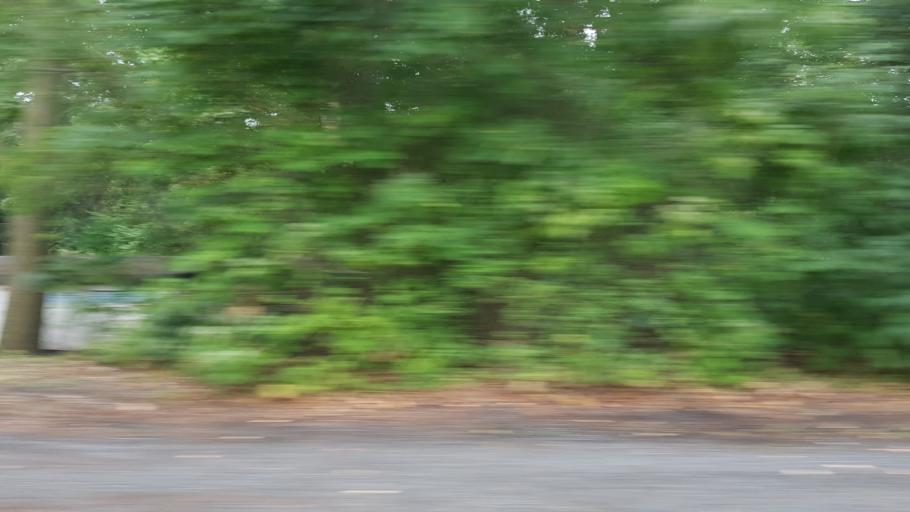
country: DE
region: Saxony
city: Heidenau
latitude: 51.0223
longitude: 13.8218
